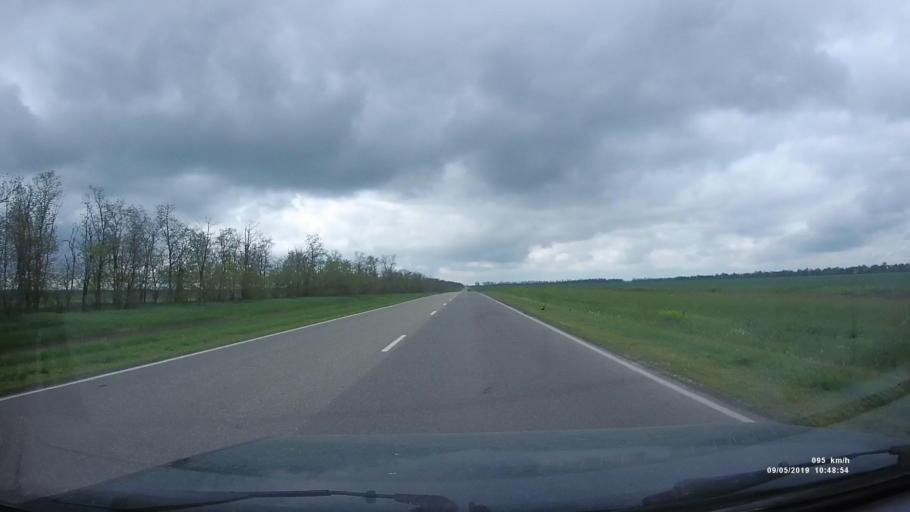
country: RU
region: Rostov
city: Peshkovo
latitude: 46.9502
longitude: 39.3552
